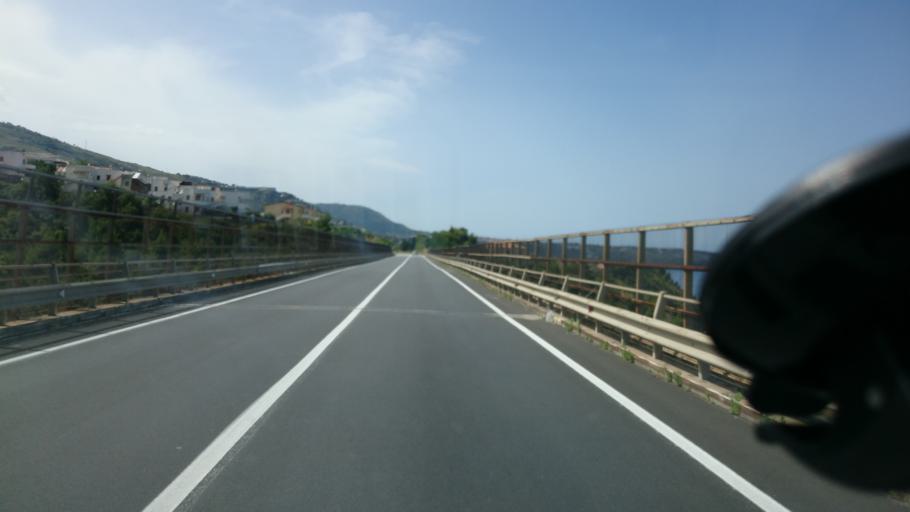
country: IT
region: Calabria
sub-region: Provincia di Cosenza
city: Praia a Mare
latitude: 39.8858
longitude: 15.7937
